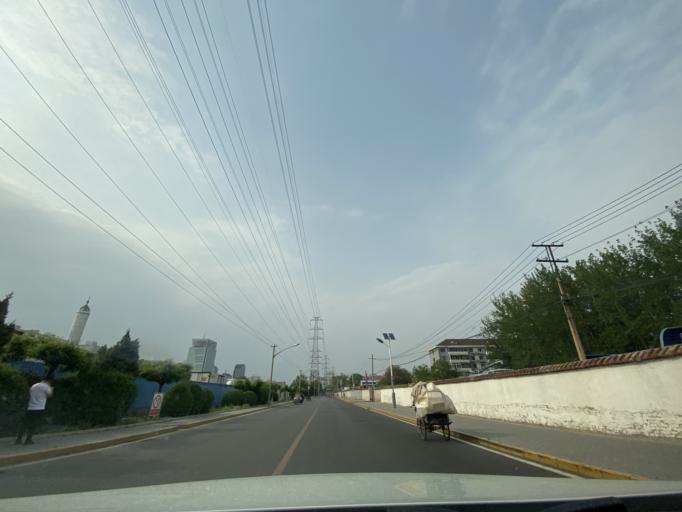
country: CN
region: Beijing
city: Haidian
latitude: 39.9785
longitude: 116.3350
